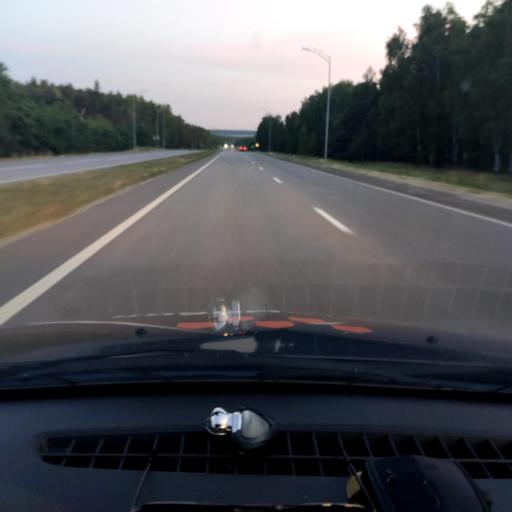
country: RU
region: Belgorod
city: Staryy Oskol
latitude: 51.3672
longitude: 37.8425
